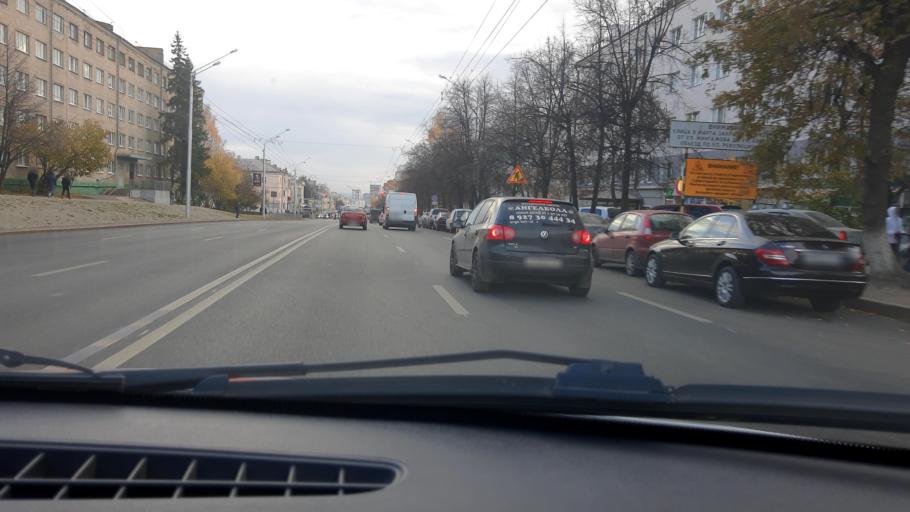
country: RU
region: Bashkortostan
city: Ufa
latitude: 54.7371
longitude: 55.9813
